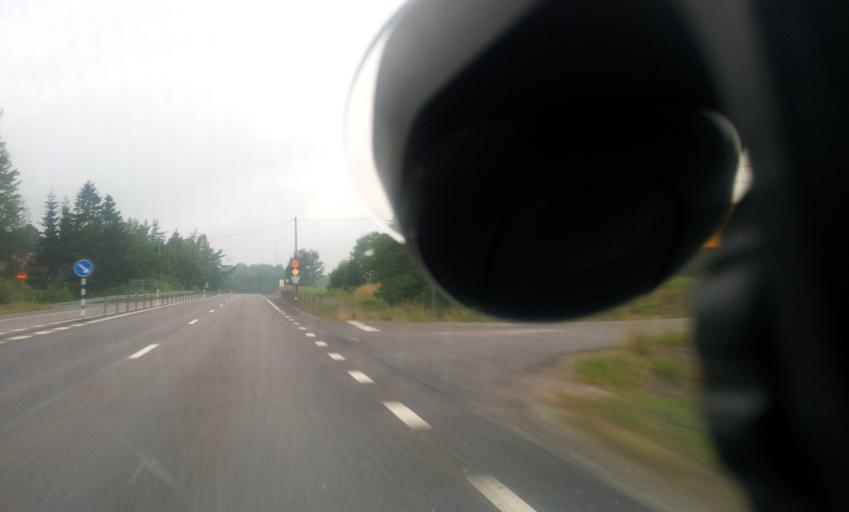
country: SE
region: Kalmar
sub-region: Vasterviks Kommun
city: Gamleby
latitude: 57.8055
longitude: 16.5022
